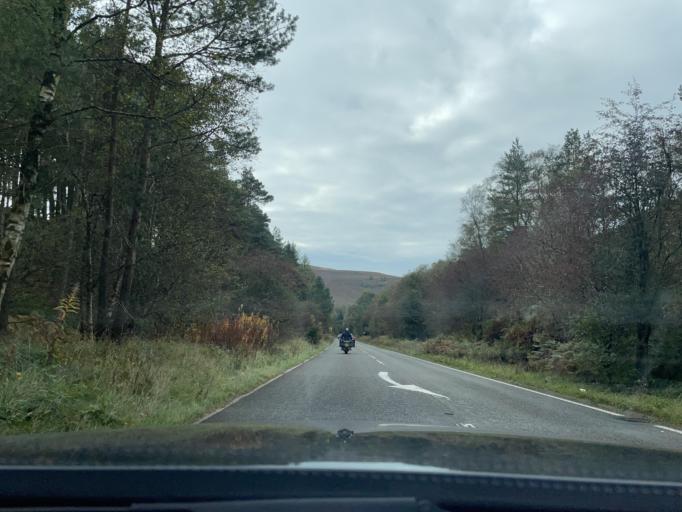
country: GB
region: England
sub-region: Derbyshire
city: Hathersage
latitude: 53.3814
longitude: -1.6822
